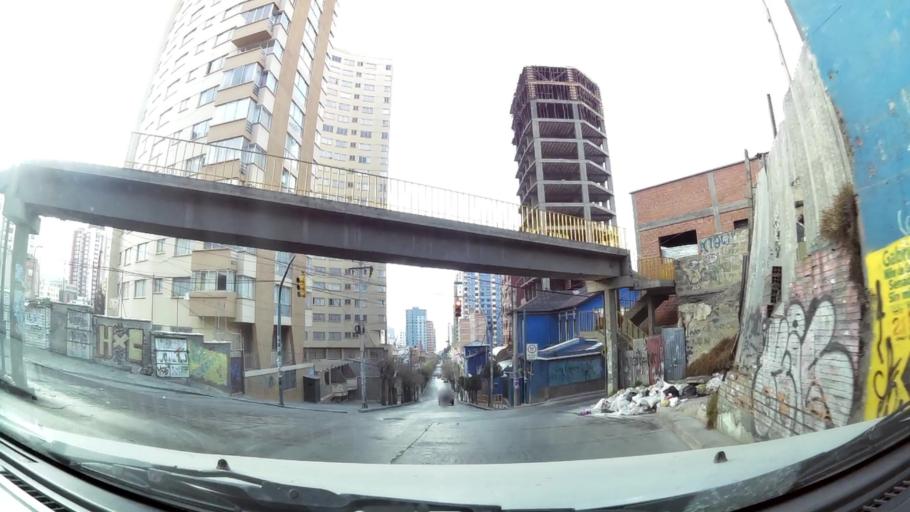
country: BO
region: La Paz
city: La Paz
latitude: -16.5069
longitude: -68.1315
